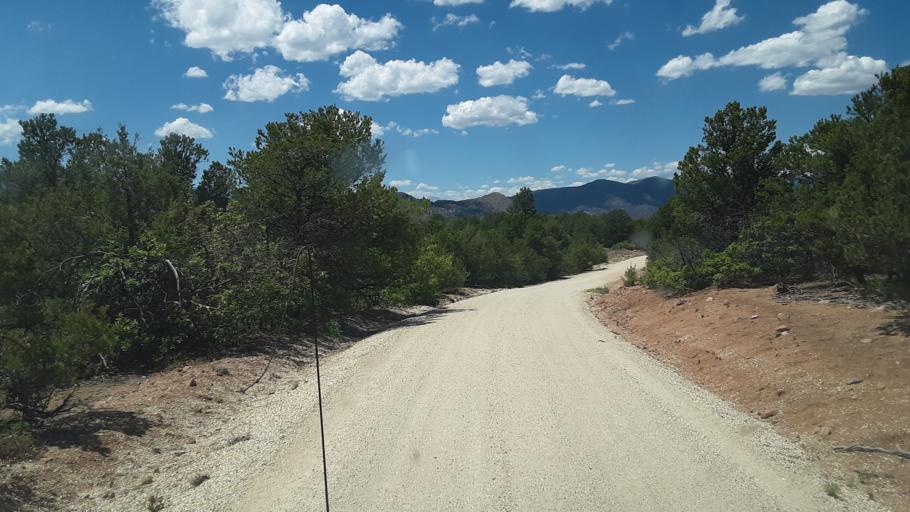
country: US
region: Colorado
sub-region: Custer County
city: Westcliffe
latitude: 38.3259
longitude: -105.6284
